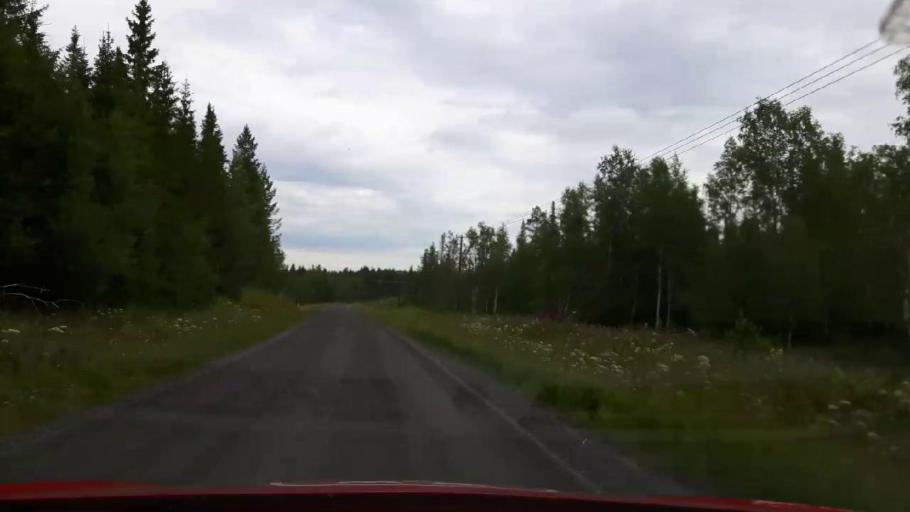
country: SE
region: Jaemtland
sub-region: Stroemsunds Kommun
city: Stroemsund
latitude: 63.4726
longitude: 15.2910
